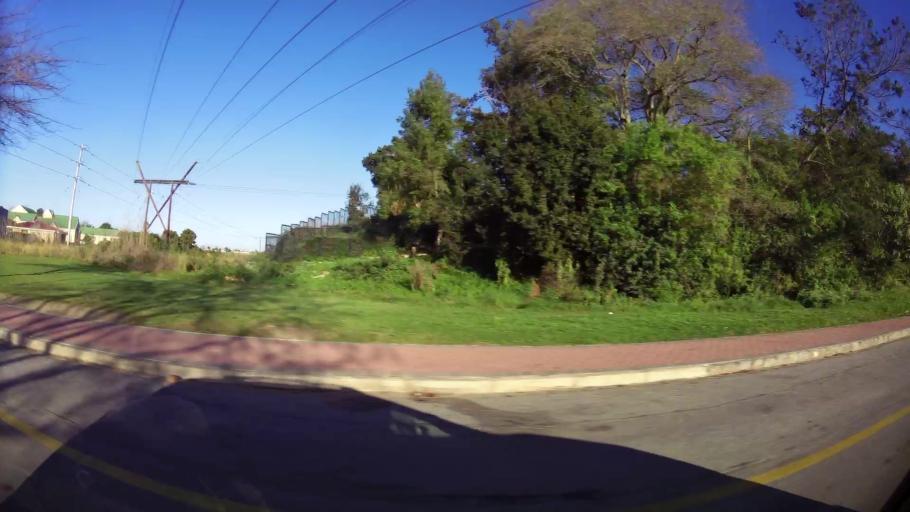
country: ZA
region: Western Cape
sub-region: Eden District Municipality
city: George
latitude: -33.9555
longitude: 22.4515
